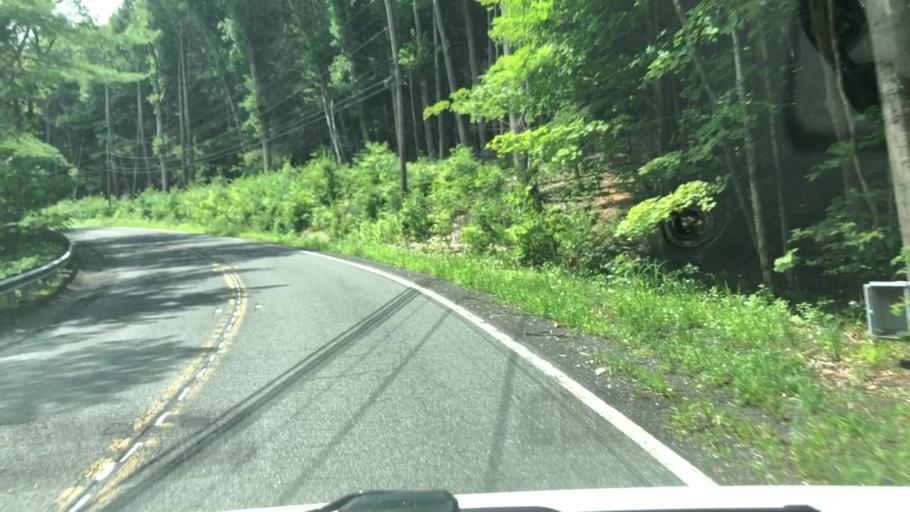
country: US
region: Massachusetts
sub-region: Franklin County
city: Conway
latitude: 42.5170
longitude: -72.7354
